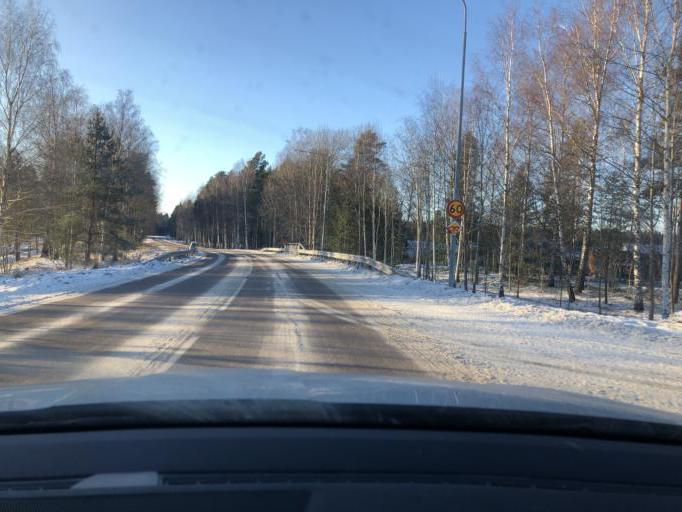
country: SE
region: Vaestmanland
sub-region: Vasteras
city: Hokasen
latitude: 59.6675
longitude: 16.5913
